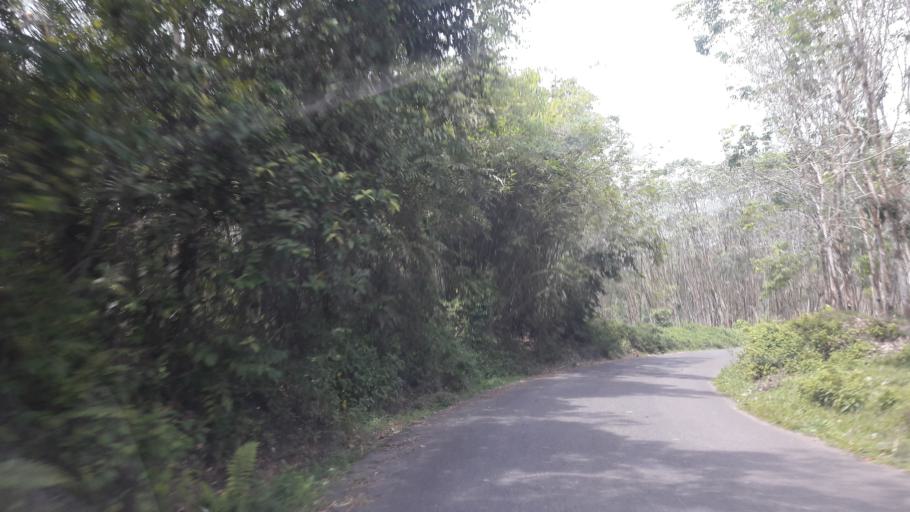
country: ID
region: South Sumatra
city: Gunungmenang
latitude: -3.1373
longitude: 104.0587
